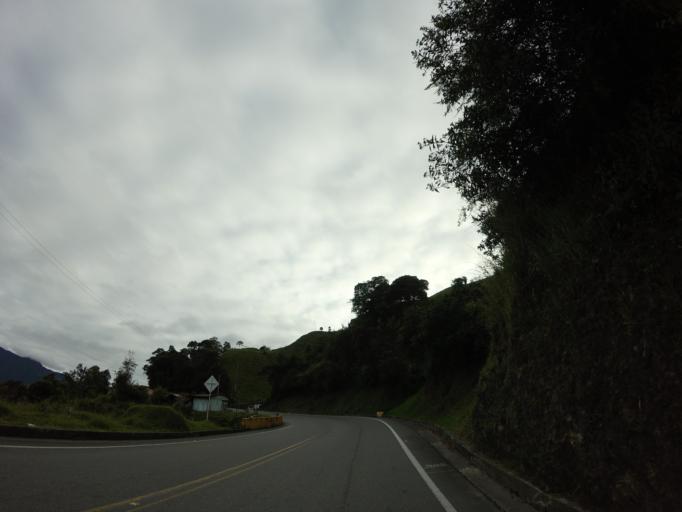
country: CO
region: Tolima
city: Herveo
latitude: 5.1022
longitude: -75.2285
